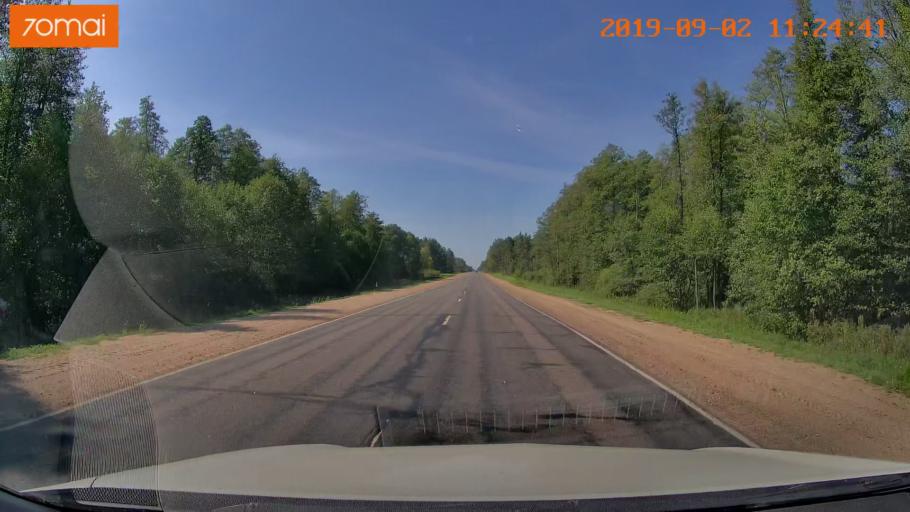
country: RU
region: Smolensk
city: Roslavl'
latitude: 54.0083
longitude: 32.9701
